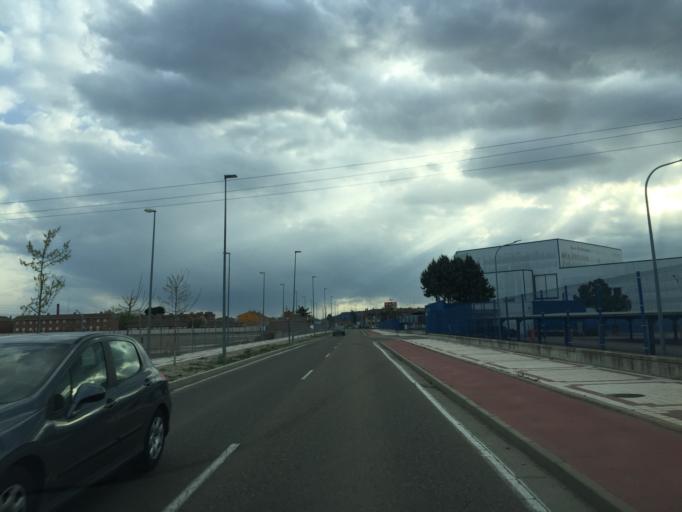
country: ES
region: Castille and Leon
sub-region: Provincia de Palencia
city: Venta de Banos
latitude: 41.9284
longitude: -4.4870
